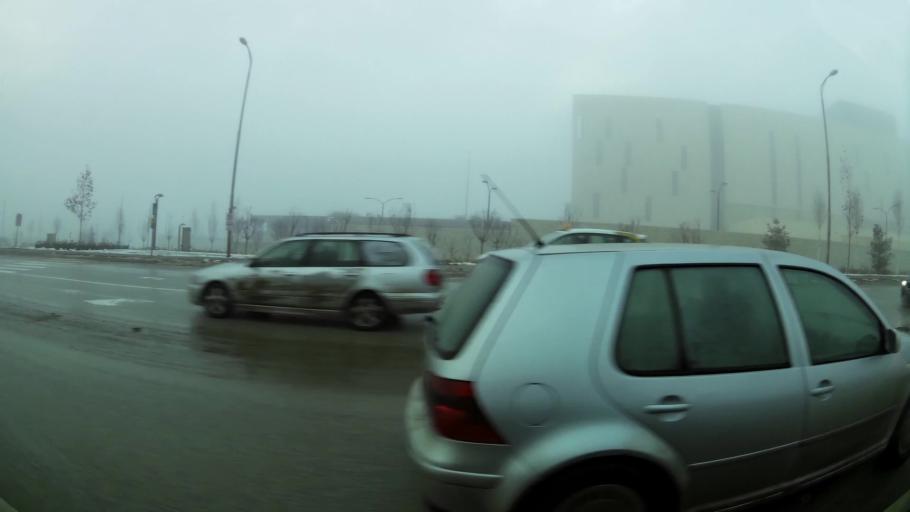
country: XK
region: Pristina
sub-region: Komuna e Prishtines
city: Pristina
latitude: 42.6569
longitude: 21.1424
